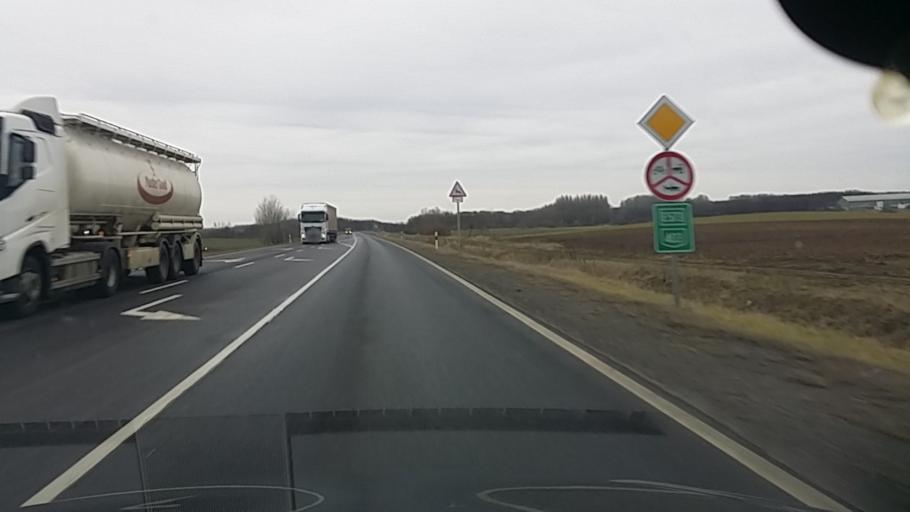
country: HU
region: Szabolcs-Szatmar-Bereg
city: Napkor
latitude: 47.9350
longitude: 21.8185
